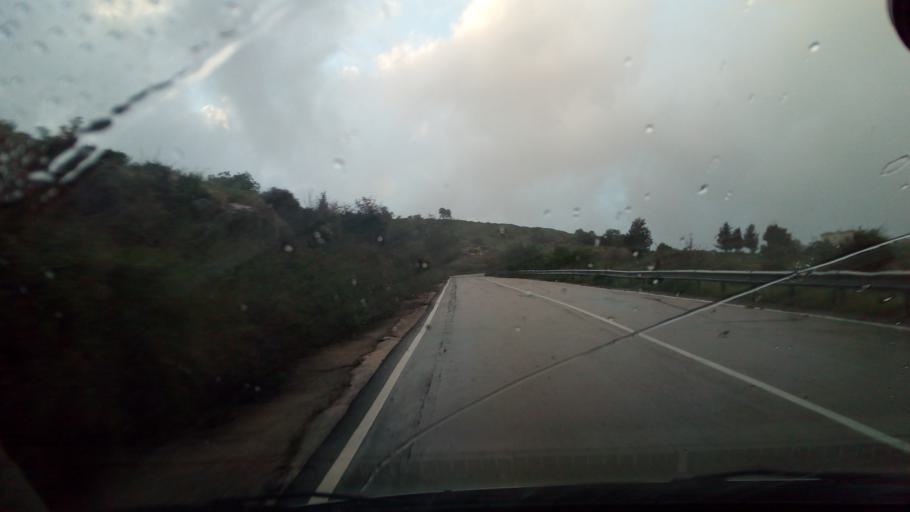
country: CY
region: Pafos
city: Pegeia
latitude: 34.9561
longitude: 32.4139
